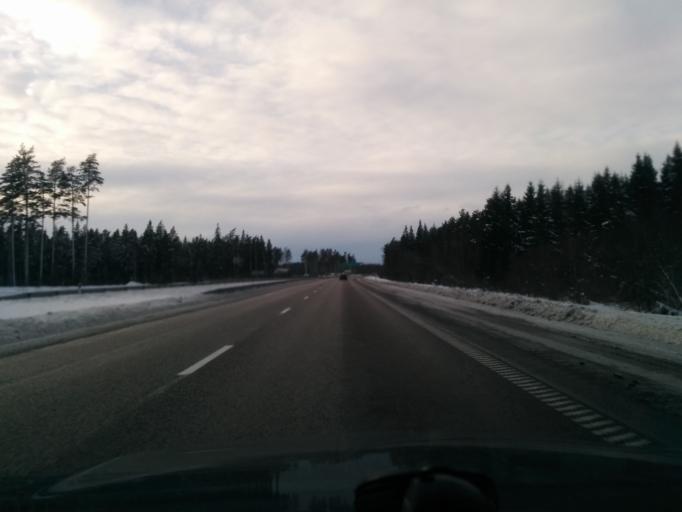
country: SE
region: Uppsala
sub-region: Enkopings Kommun
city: Enkoping
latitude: 59.6462
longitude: 17.1622
